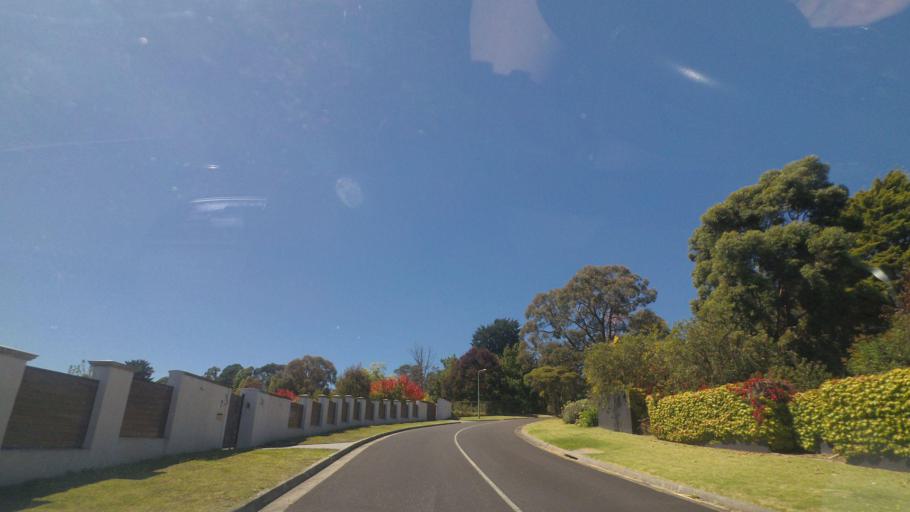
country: AU
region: Victoria
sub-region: Manningham
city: Donvale
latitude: -37.7922
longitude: 145.1844
